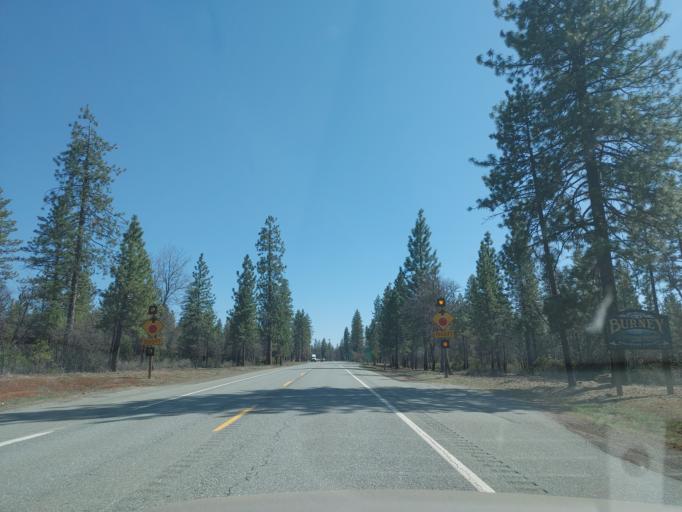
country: US
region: California
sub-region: Shasta County
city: Burney
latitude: 40.9421
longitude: -121.6082
